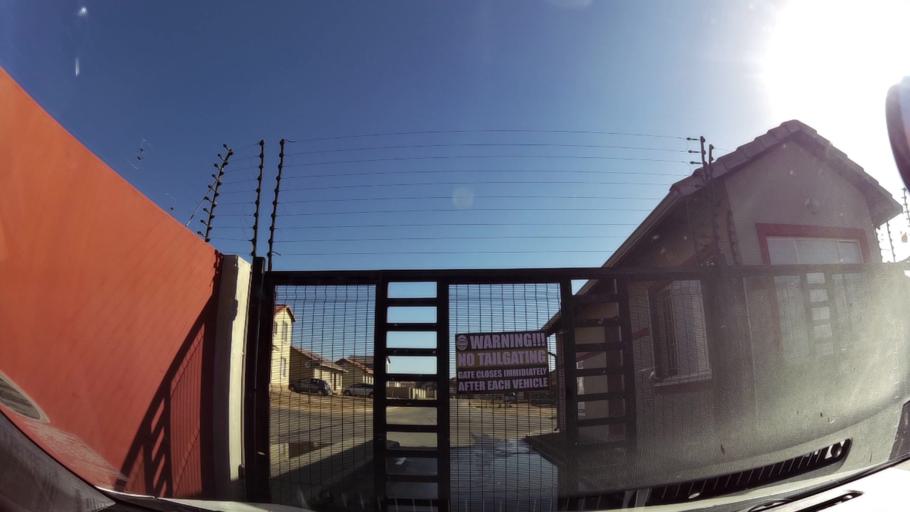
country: ZA
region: Gauteng
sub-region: City of Johannesburg Metropolitan Municipality
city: Diepsloot
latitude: -26.0190
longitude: 27.9673
